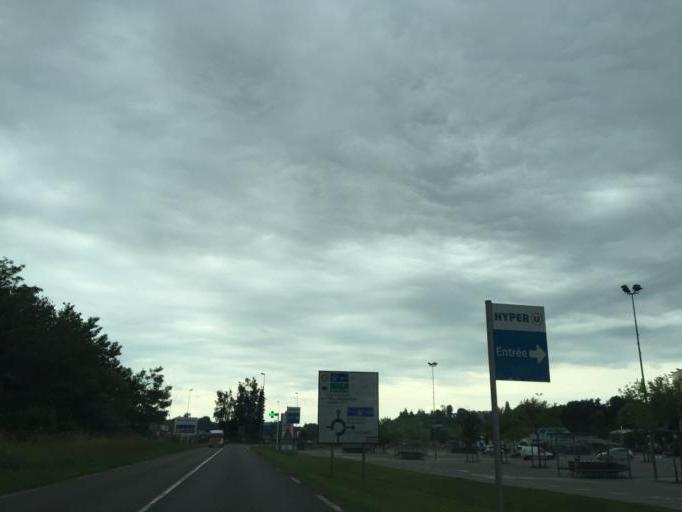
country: FR
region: Rhone-Alpes
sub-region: Departement de la Savoie
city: Domessin
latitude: 45.5283
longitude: 5.6912
